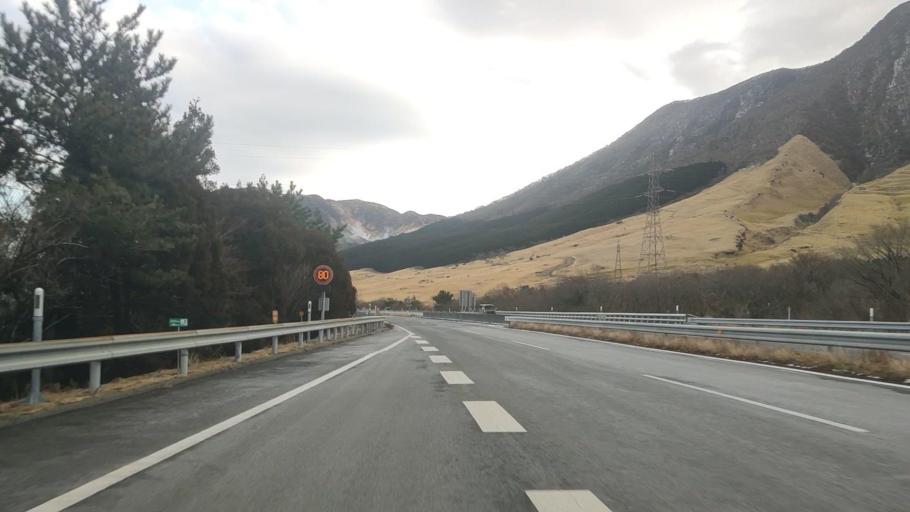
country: JP
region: Oita
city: Beppu
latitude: 33.3039
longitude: 131.4005
